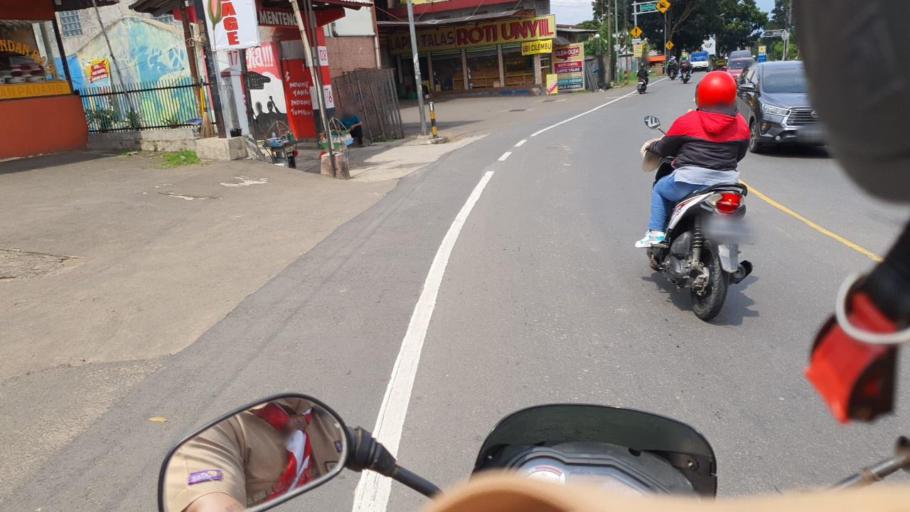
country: ID
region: West Java
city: Caringin
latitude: -6.6537
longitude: 106.8786
